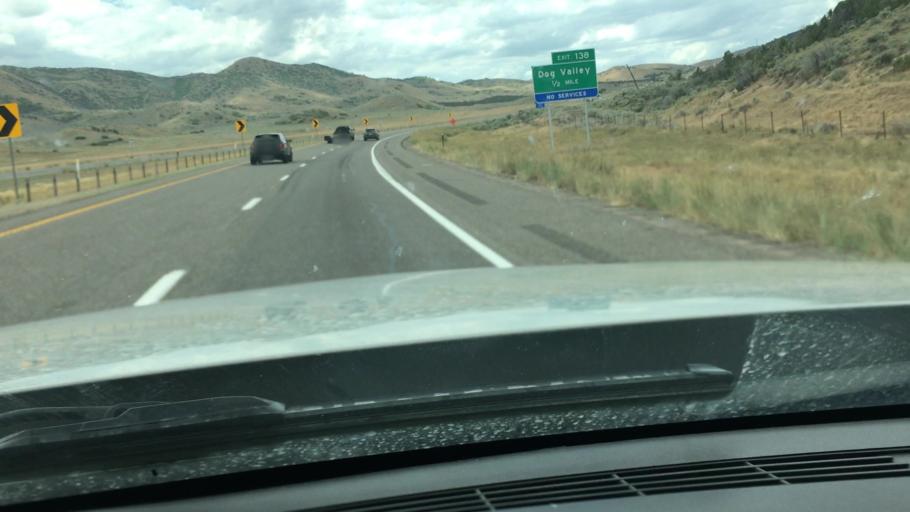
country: US
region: Utah
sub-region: Beaver County
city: Beaver
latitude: 38.6688
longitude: -112.5902
